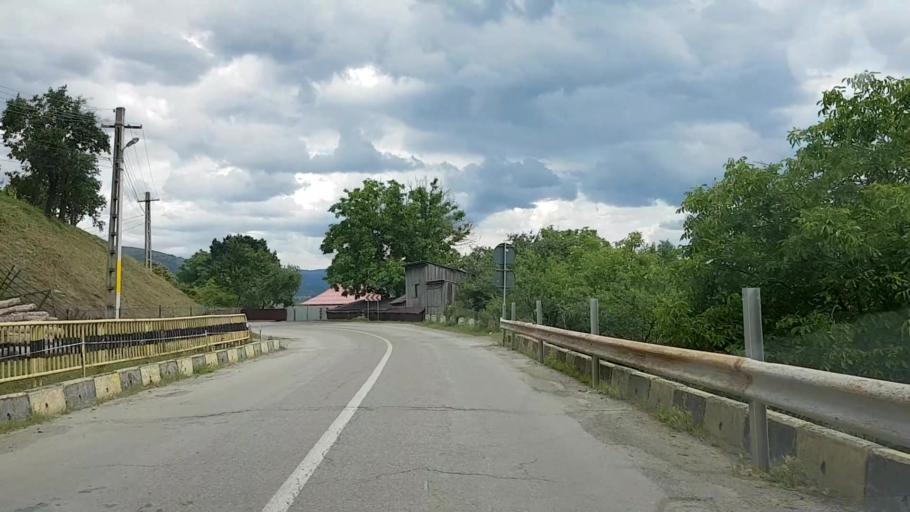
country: RO
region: Neamt
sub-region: Comuna Hangu
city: Hangu
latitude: 47.0526
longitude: 26.0261
